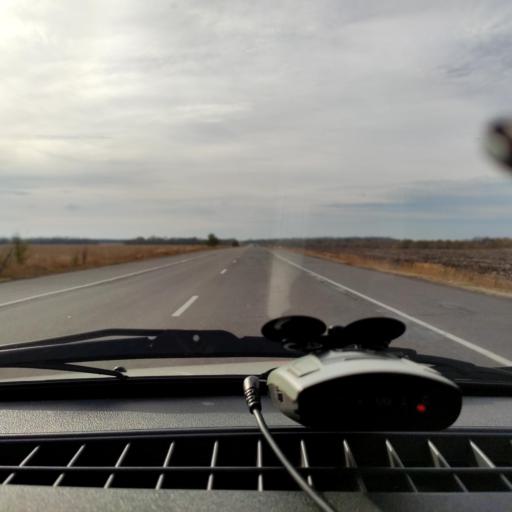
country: RU
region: Voronezj
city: Devitsa
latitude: 51.5873
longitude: 38.9768
